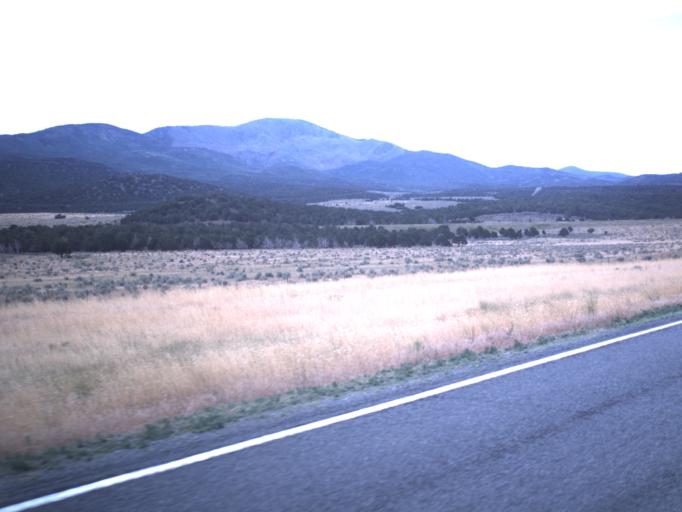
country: US
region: Utah
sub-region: Beaver County
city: Beaver
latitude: 38.5947
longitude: -112.5815
